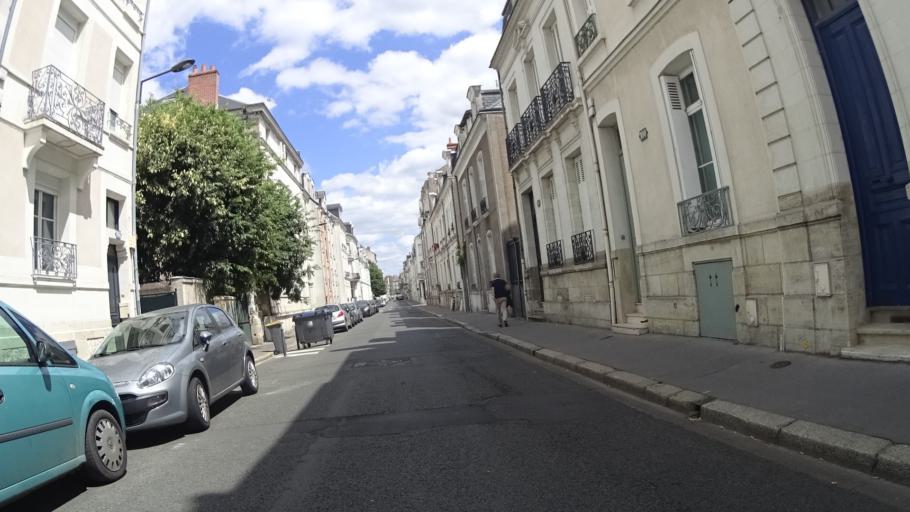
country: FR
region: Centre
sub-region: Departement d'Indre-et-Loire
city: Tours
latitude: 47.3871
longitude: 0.6828
